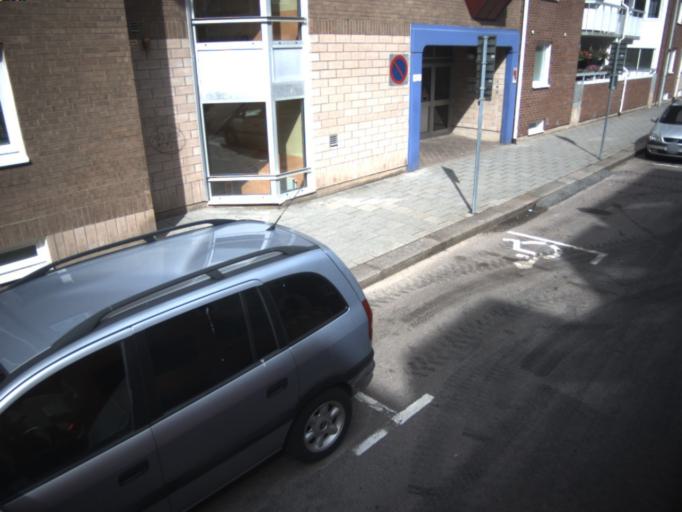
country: SE
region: Skane
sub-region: Helsingborg
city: Helsingborg
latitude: 56.0380
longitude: 12.7053
